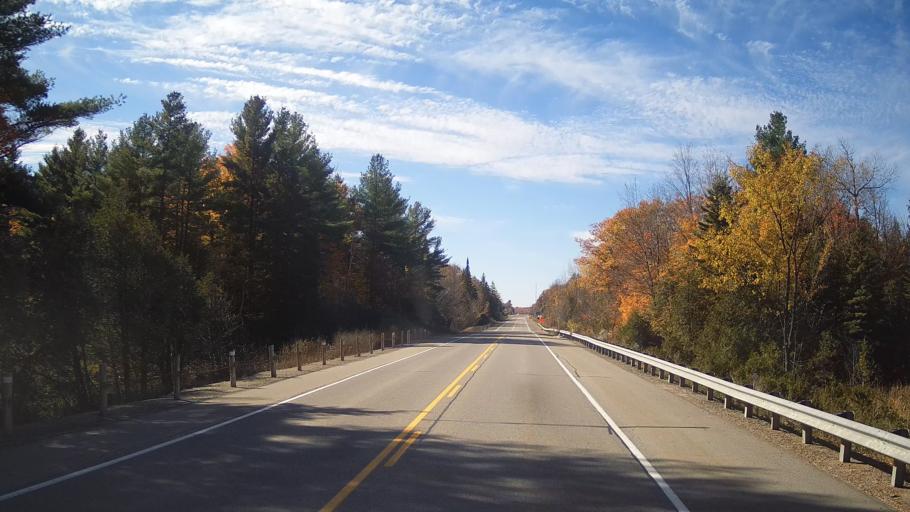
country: CA
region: Ontario
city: Perth
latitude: 44.8010
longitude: -76.6689
